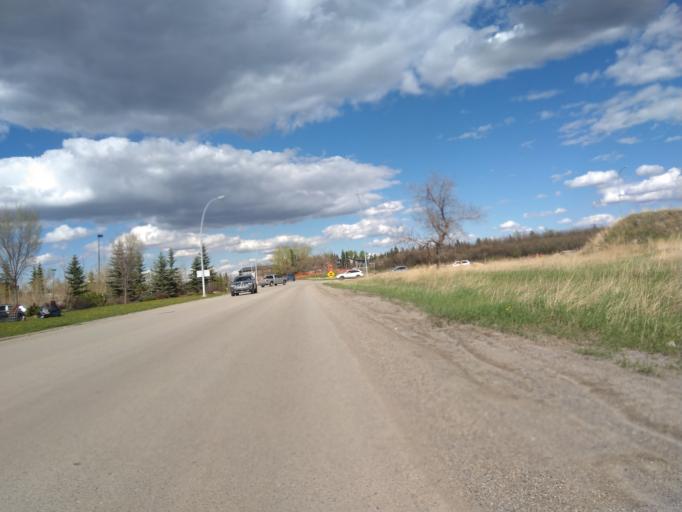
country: CA
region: Alberta
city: Calgary
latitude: 51.0057
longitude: -114.1467
